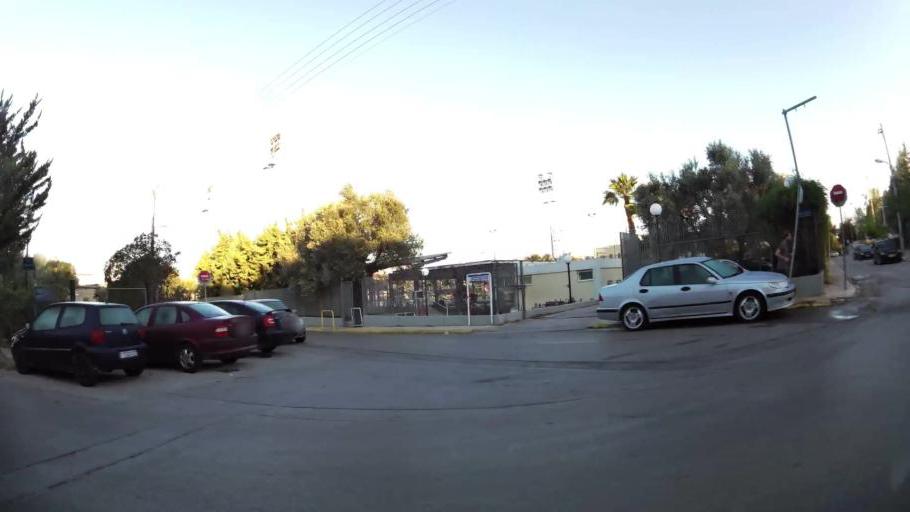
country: GR
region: Attica
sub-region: Nomarchia Athinas
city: Vrilissia
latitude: 38.0410
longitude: 23.8229
